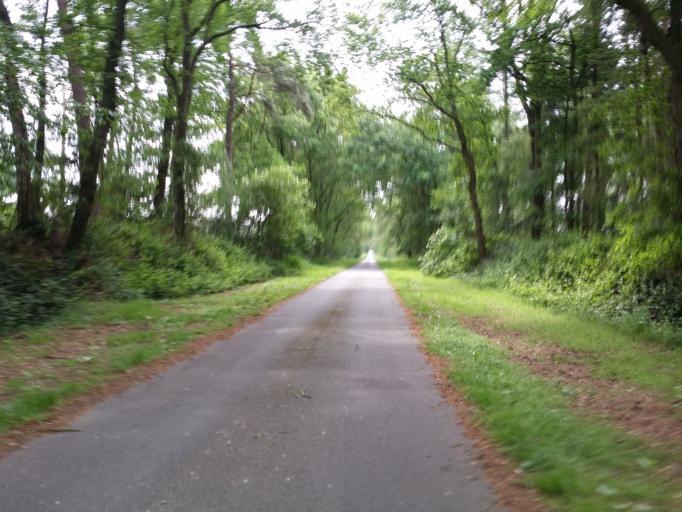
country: DE
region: Lower Saxony
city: Friedeburg
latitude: 53.4893
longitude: 7.8189
